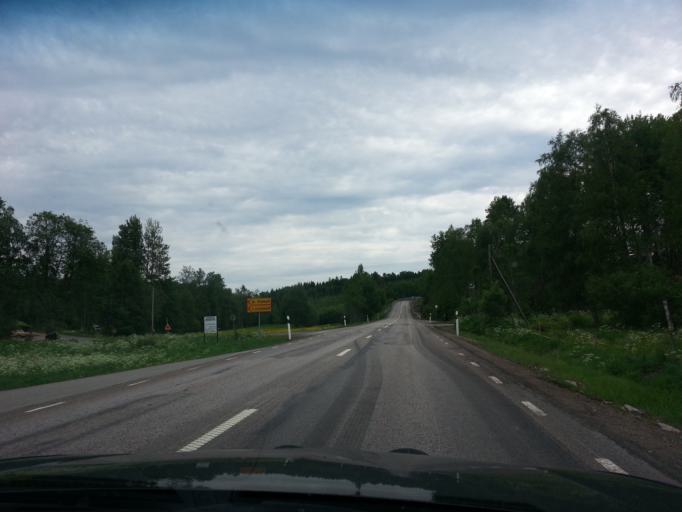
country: SE
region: Joenkoeping
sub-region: Vetlanda Kommun
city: Vetlanda
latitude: 57.2869
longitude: 15.1315
